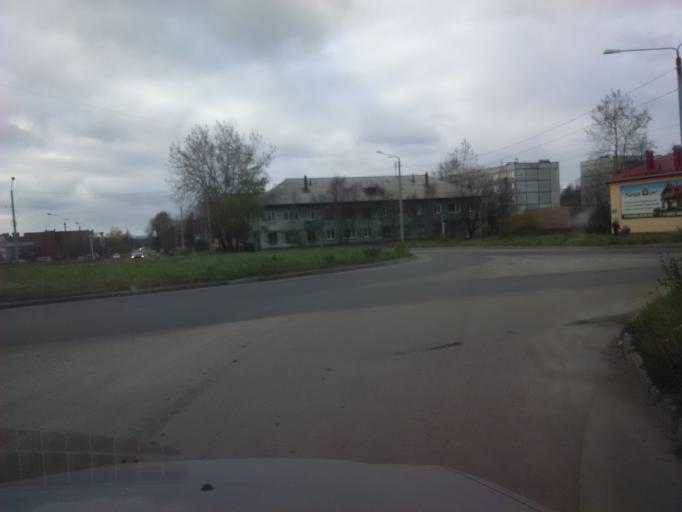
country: RU
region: Murmansk
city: Kandalaksha
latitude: 67.1566
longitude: 32.4028
